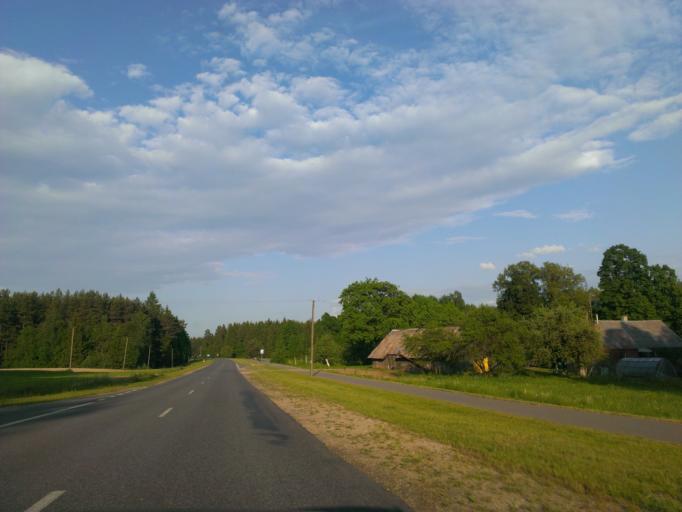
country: LT
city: Plateliai
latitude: 56.0620
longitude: 21.8705
